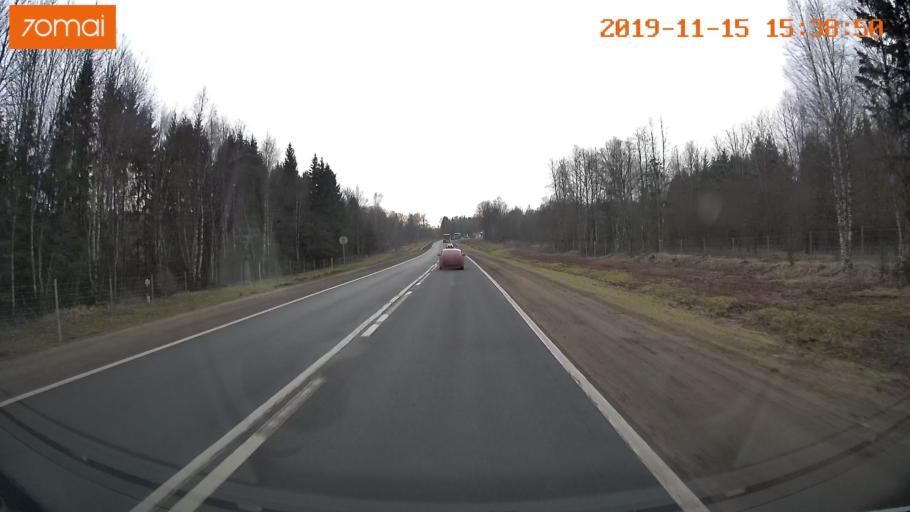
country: RU
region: Jaroslavl
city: Danilov
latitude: 58.0262
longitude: 40.0757
